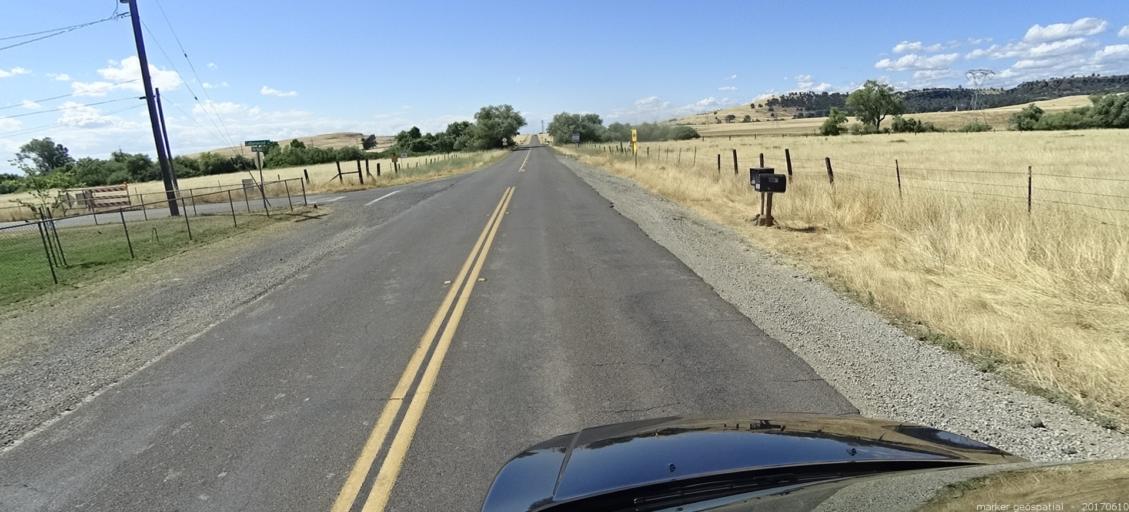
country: US
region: California
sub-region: Butte County
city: Thermalito
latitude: 39.5577
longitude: -121.5982
